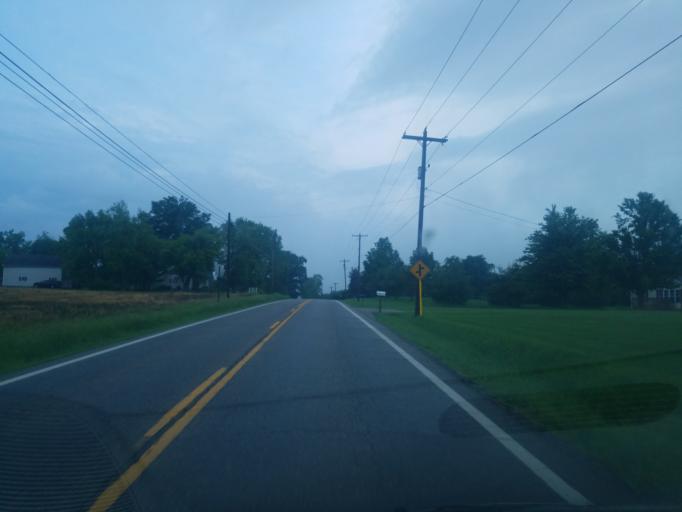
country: US
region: Ohio
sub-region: Columbiana County
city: Salem
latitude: 40.8527
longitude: -80.8919
